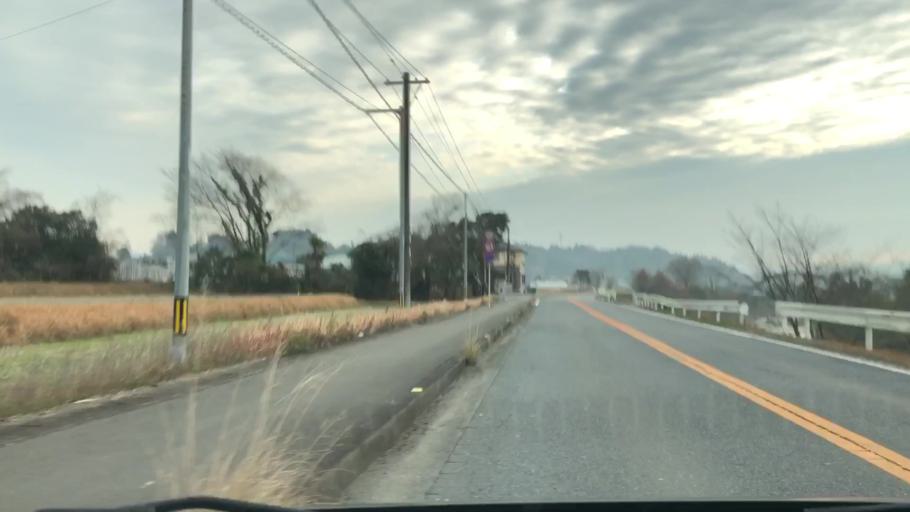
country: JP
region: Oita
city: Takedamachi
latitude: 32.9696
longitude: 131.4690
